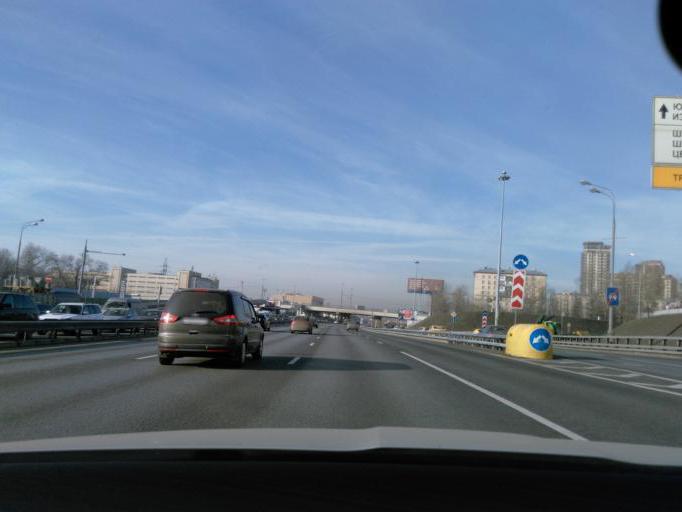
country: RU
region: Moskovskaya
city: Kozhukhovo
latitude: 55.7153
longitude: 37.6836
